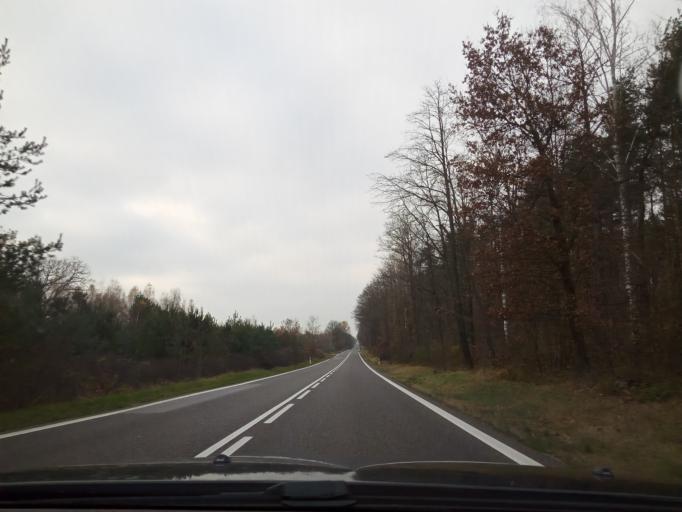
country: PL
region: Swietokrzyskie
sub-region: Powiat jedrzejowski
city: Imielno
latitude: 50.6158
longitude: 20.4619
